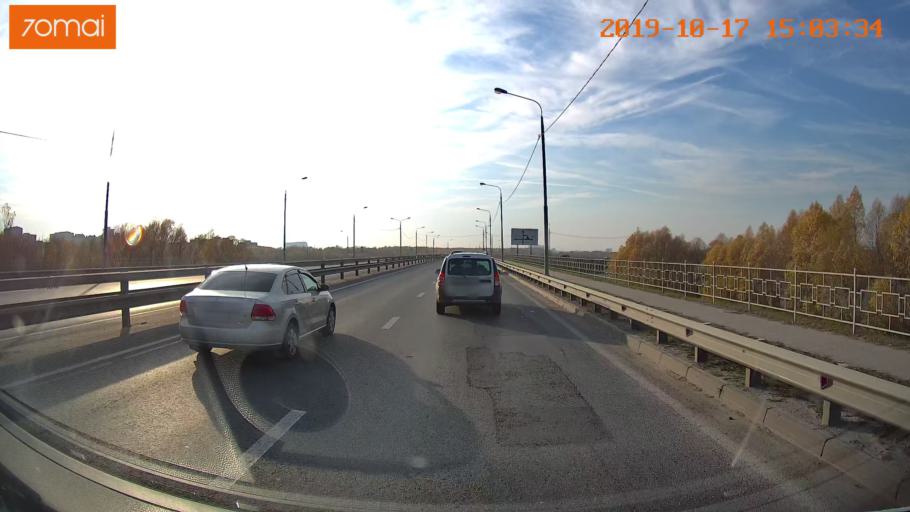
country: RU
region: Rjazan
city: Ryazan'
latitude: 54.6408
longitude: 39.7244
